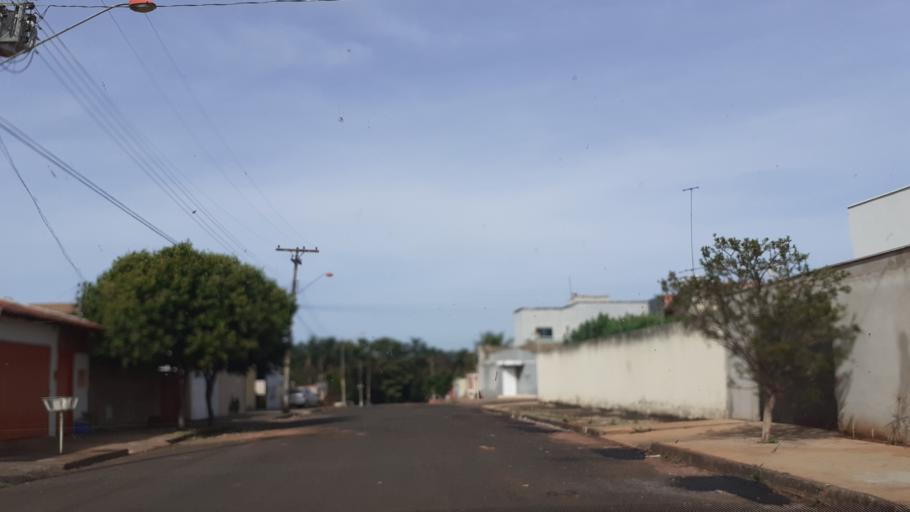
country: BR
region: Goias
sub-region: Itumbiara
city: Itumbiara
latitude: -18.4236
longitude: -49.2420
